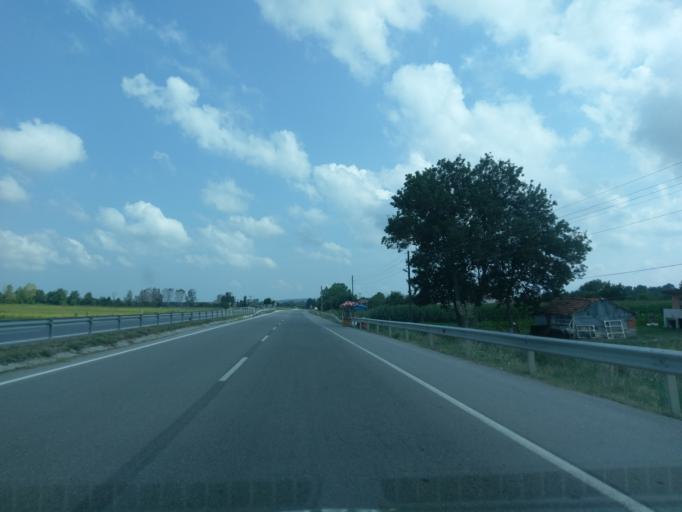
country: TR
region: Samsun
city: Bafra
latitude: 41.5992
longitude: 35.7738
